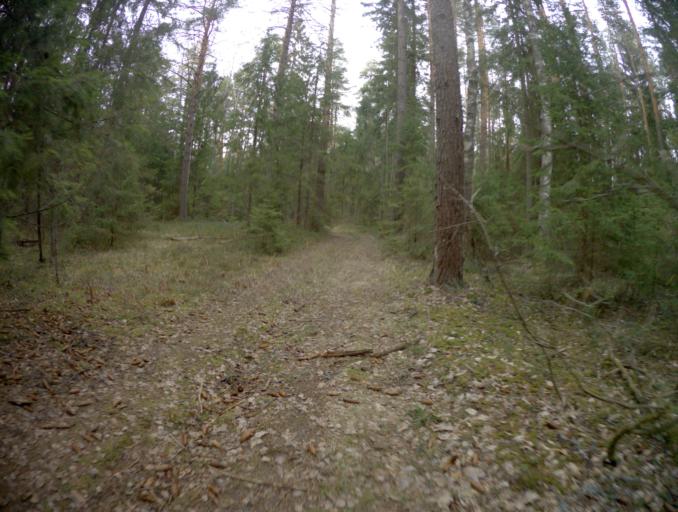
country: RU
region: Vladimir
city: Kommunar
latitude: 56.0780
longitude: 40.5231
